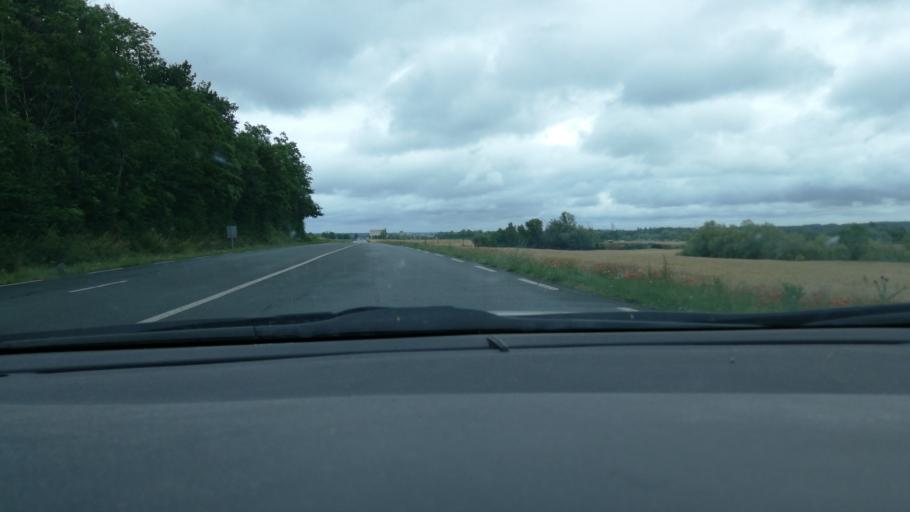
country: FR
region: Poitou-Charentes
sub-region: Departement de la Vienne
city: Naintre
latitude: 46.7390
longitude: 0.4663
